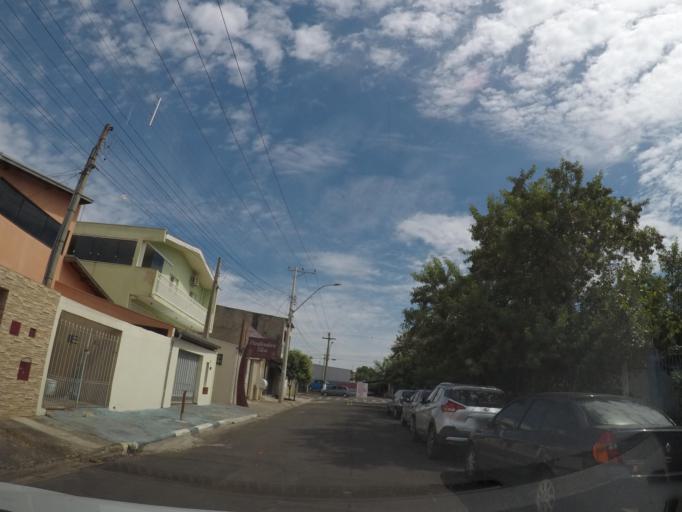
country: BR
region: Sao Paulo
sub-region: Hortolandia
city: Hortolandia
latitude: -22.8342
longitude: -47.1858
